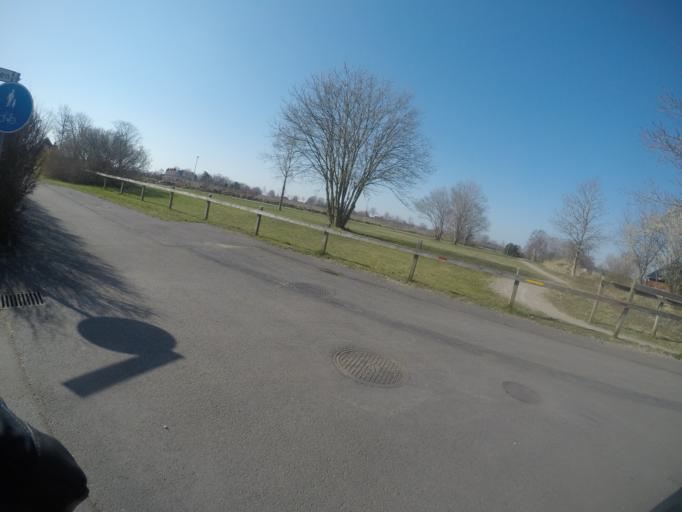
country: SE
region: Halland
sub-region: Laholms Kommun
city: Laholm
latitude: 56.5010
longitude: 13.0410
